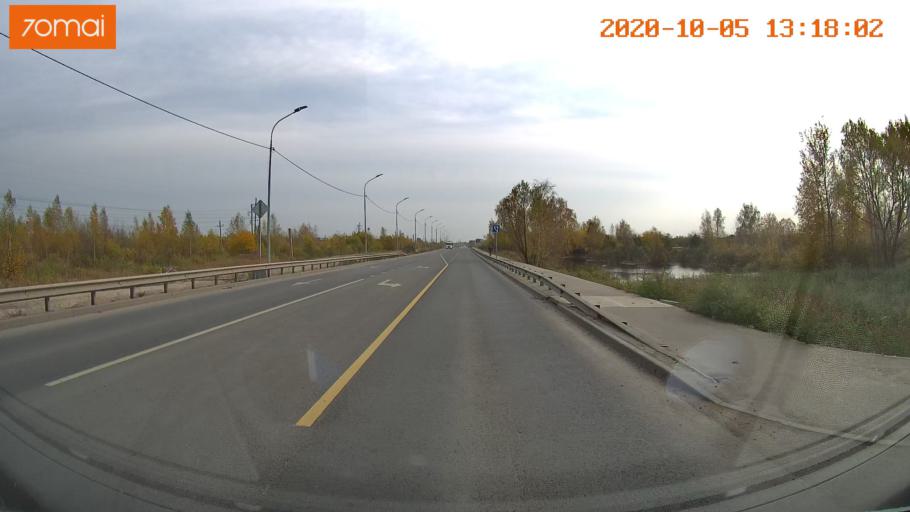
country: RU
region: Ivanovo
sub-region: Gorod Ivanovo
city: Ivanovo
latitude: 56.9809
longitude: 40.9159
